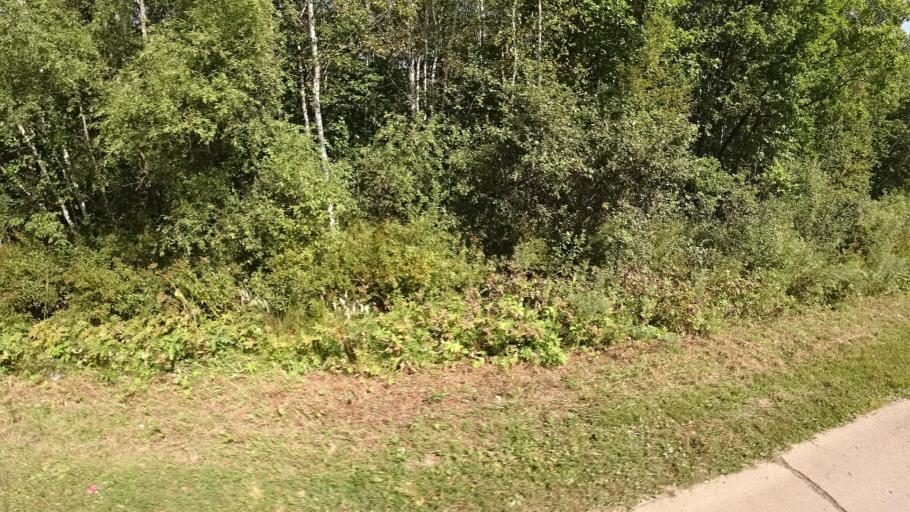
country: RU
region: Khabarovsk Krai
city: Khor
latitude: 47.9803
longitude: 135.0989
